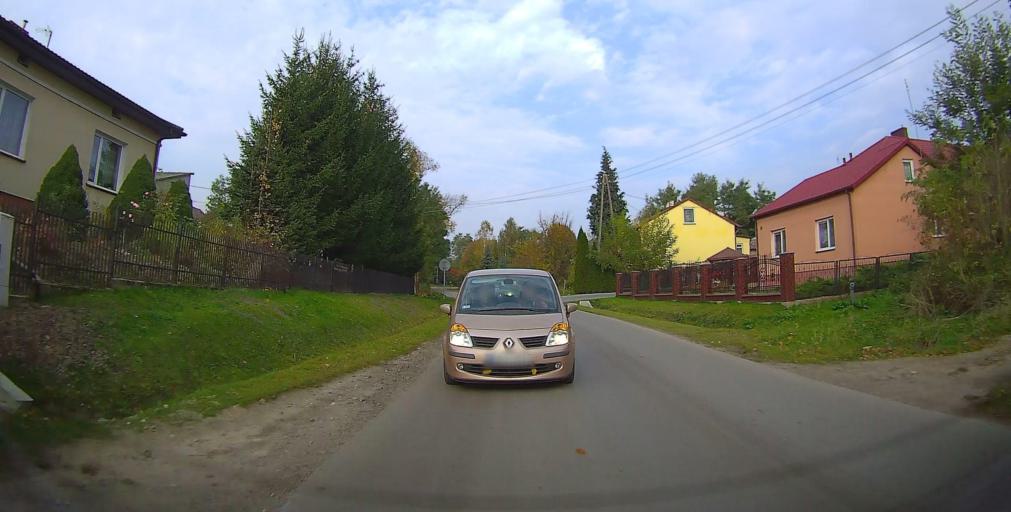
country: PL
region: Masovian Voivodeship
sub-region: Powiat grojecki
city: Mogielnica
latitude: 51.6428
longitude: 20.7410
